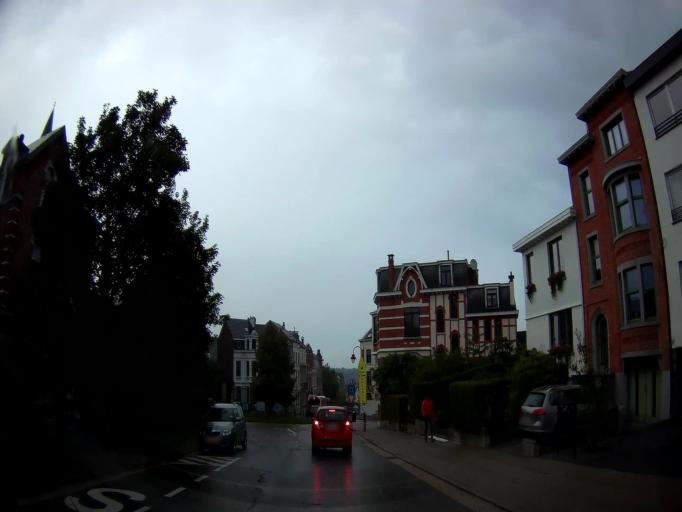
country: BE
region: Wallonia
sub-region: Province de Liege
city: Verviers
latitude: 50.5862
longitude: 5.8636
